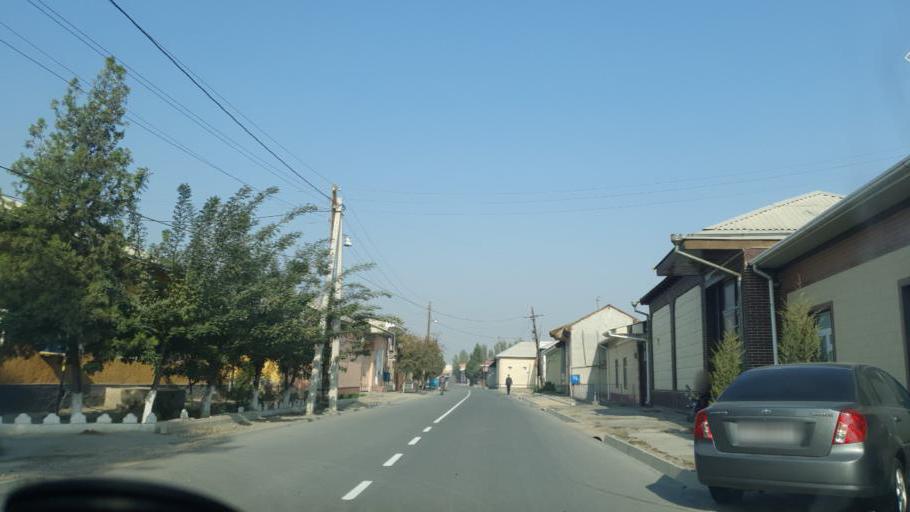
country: UZ
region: Fergana
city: Qo`qon
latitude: 40.5801
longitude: 70.9131
